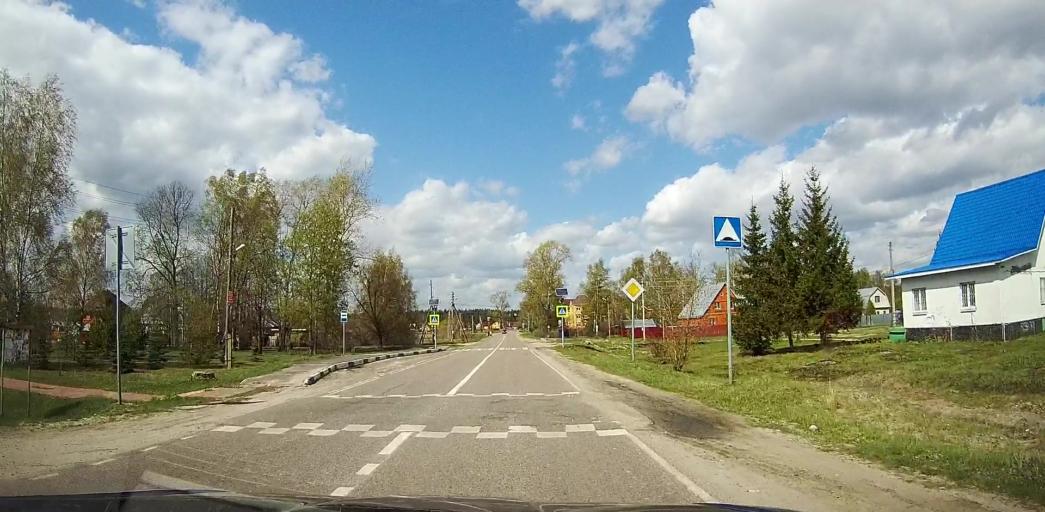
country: RU
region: Moskovskaya
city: Davydovo
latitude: 55.5561
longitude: 38.8145
